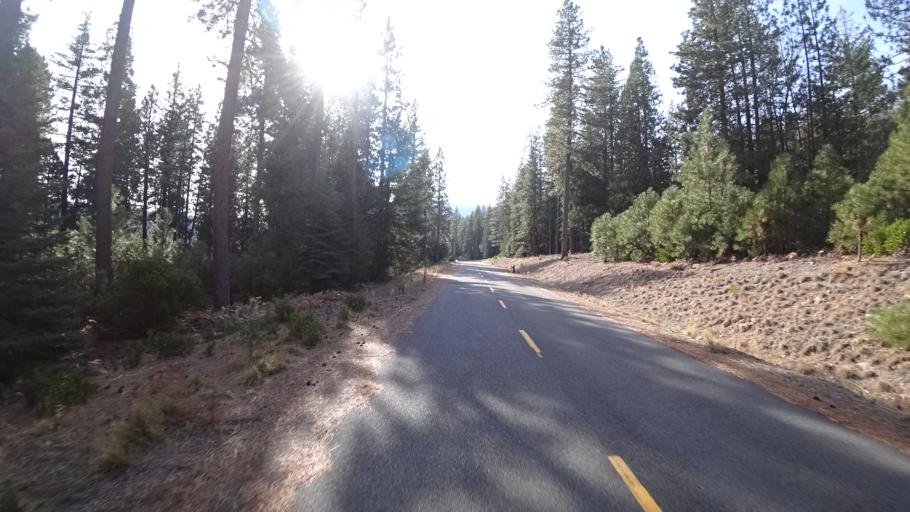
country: US
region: California
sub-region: Siskiyou County
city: Weed
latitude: 41.4015
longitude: -122.3878
